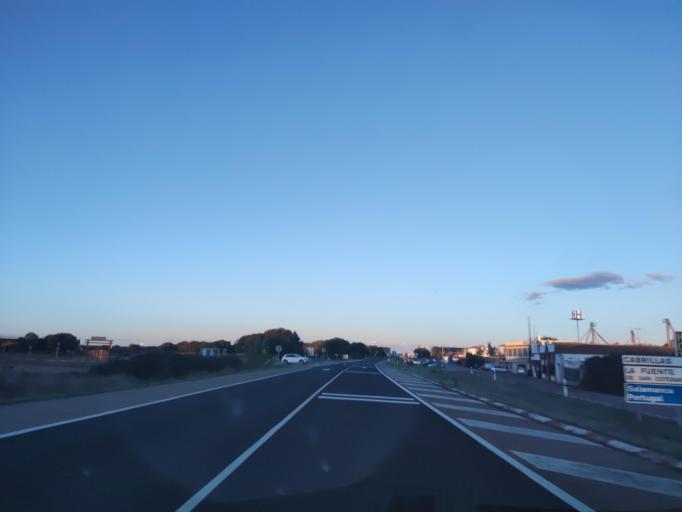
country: ES
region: Castille and Leon
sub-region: Provincia de Salamanca
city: La Fuente de San Esteban
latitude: 40.7914
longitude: -6.2455
